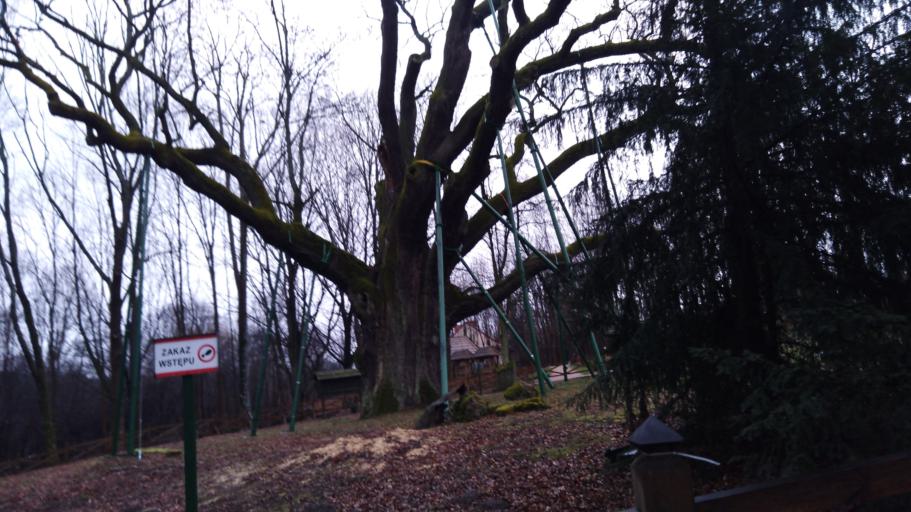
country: PL
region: Swietokrzyskie
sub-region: Powiat kielecki
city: Kaniow
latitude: 50.9876
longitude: 20.6497
